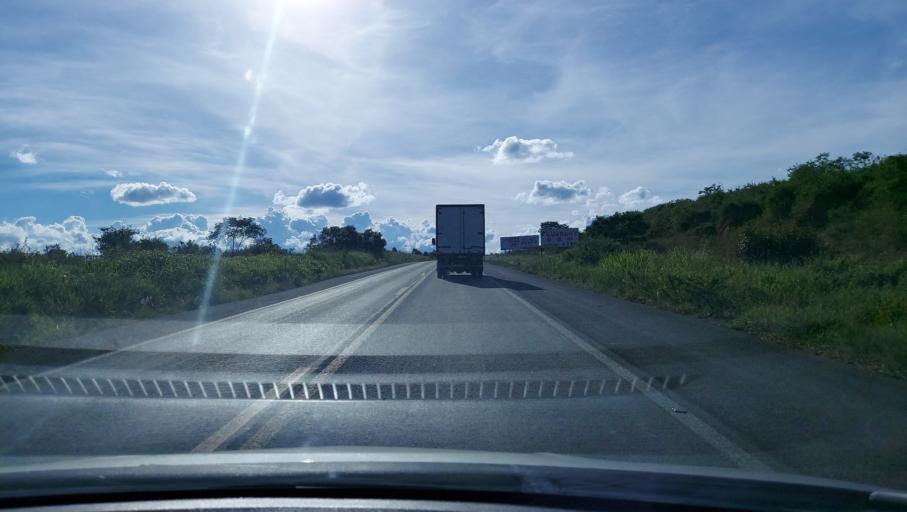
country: BR
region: Bahia
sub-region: Seabra
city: Seabra
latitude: -12.4348
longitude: -41.8190
